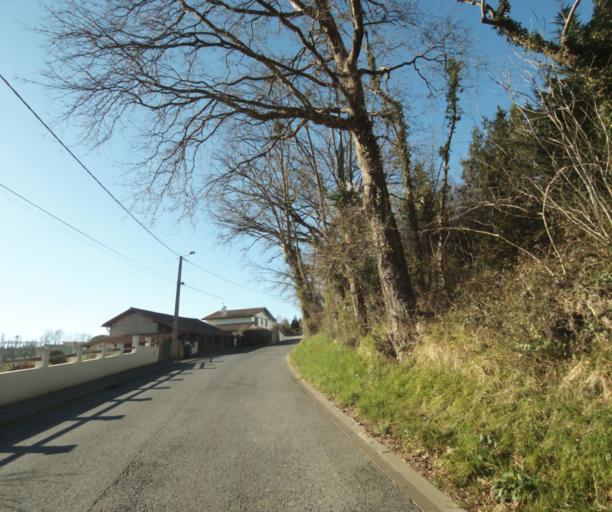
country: FR
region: Aquitaine
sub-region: Departement des Pyrenees-Atlantiques
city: Hendaye
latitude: 43.3610
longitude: -1.7556
